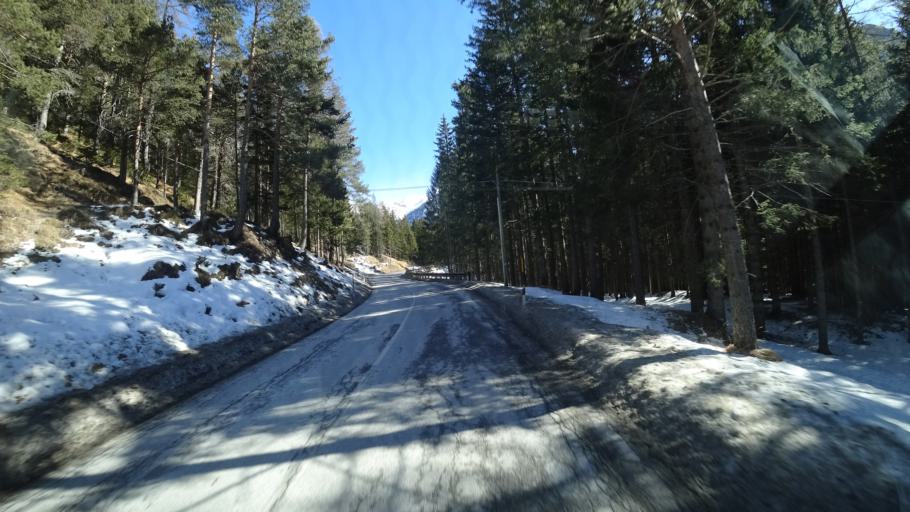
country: IT
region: Veneto
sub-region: Provincia di Belluno
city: Cortina d'Ampezzo
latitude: 46.5996
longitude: 12.1155
